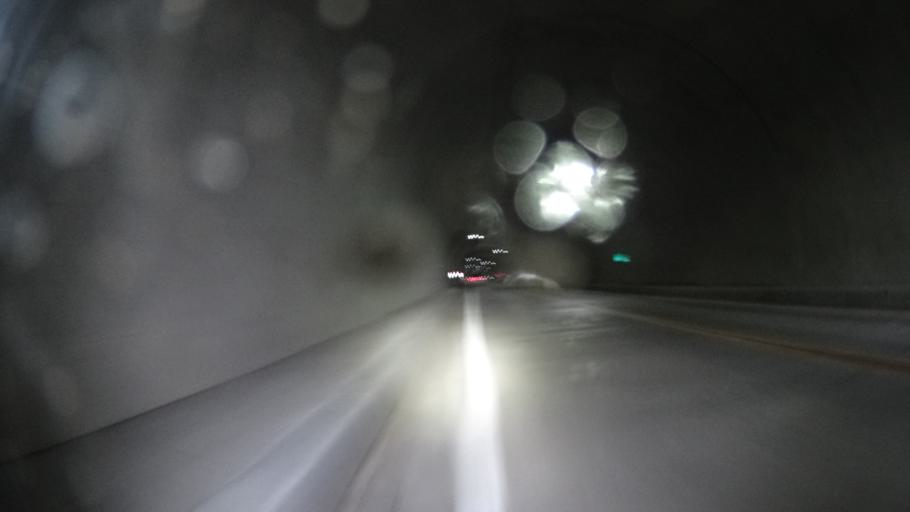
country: JP
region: Yamanashi
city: Enzan
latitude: 35.8008
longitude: 138.8651
